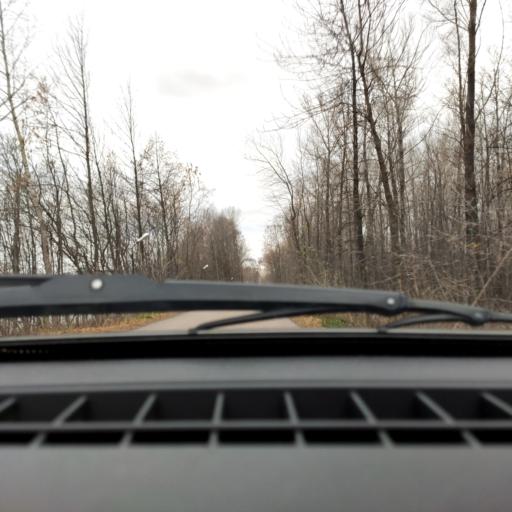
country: RU
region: Bashkortostan
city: Ufa
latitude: 54.7877
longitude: 56.0966
